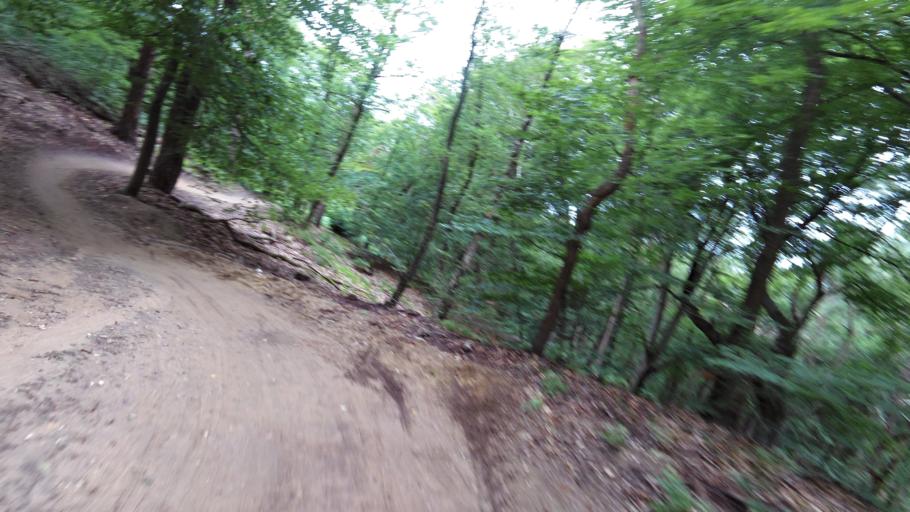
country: NL
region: Utrecht
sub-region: Gemeente Utrechtse Heuvelrug
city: Amerongen
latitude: 52.0082
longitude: 5.4729
